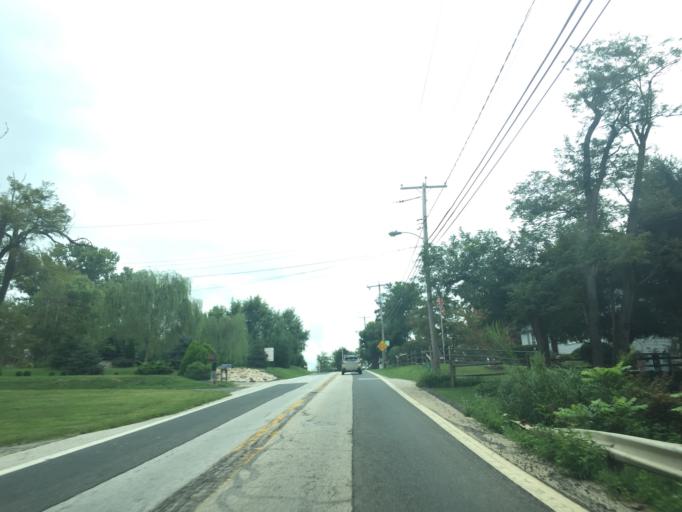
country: US
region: Maryland
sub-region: Baltimore County
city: Kingsville
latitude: 39.4179
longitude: -76.3992
